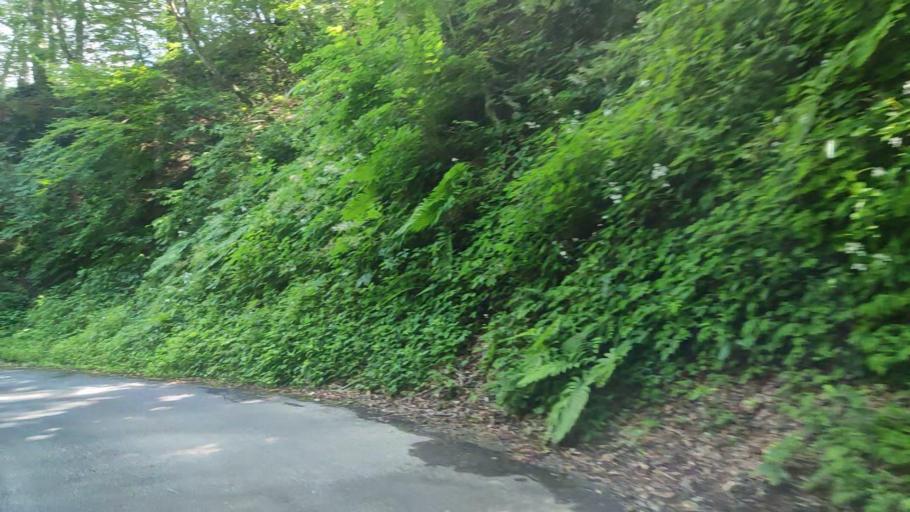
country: JP
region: Fukui
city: Ono
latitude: 35.7675
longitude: 136.5364
